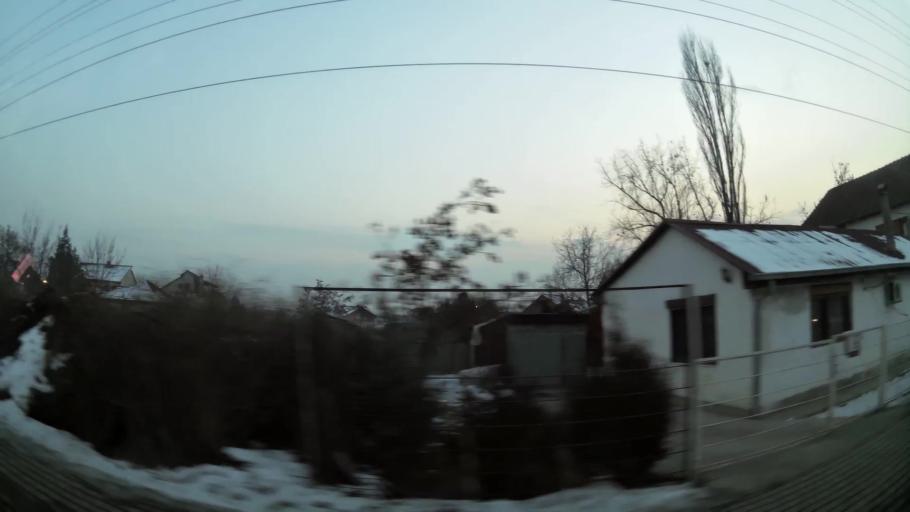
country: MK
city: Creshevo
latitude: 42.0043
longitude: 21.5128
